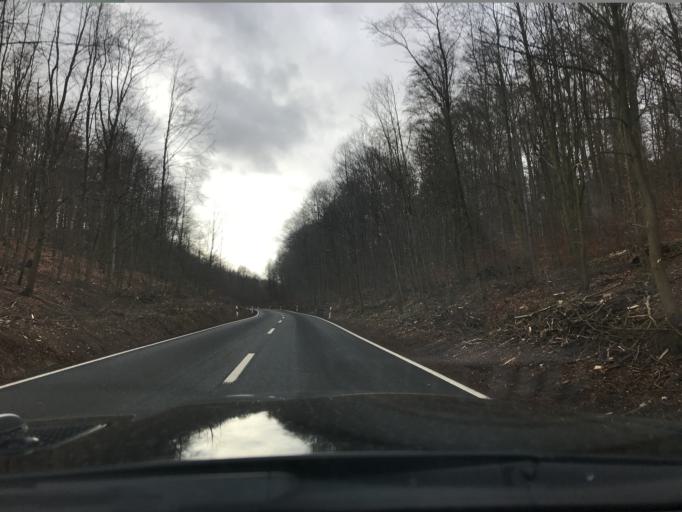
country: DE
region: Thuringia
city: Langula
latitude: 51.1393
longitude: 10.3842
